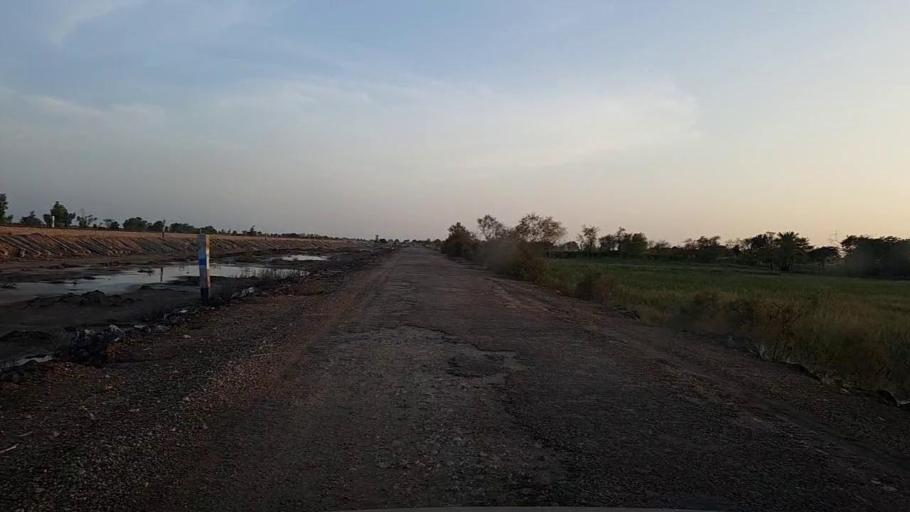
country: PK
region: Sindh
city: Karaundi
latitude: 27.0547
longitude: 68.3895
